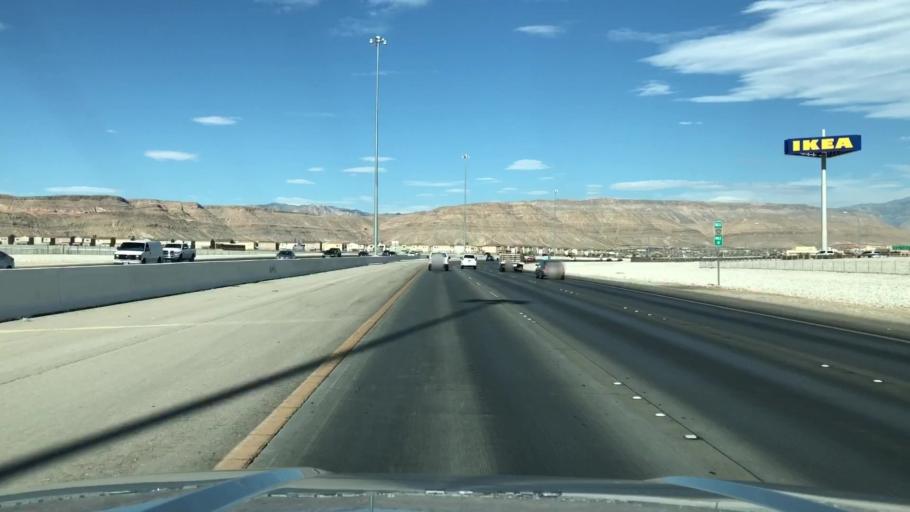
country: US
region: Nevada
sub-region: Clark County
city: Spring Valley
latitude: 36.0663
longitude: -115.2804
